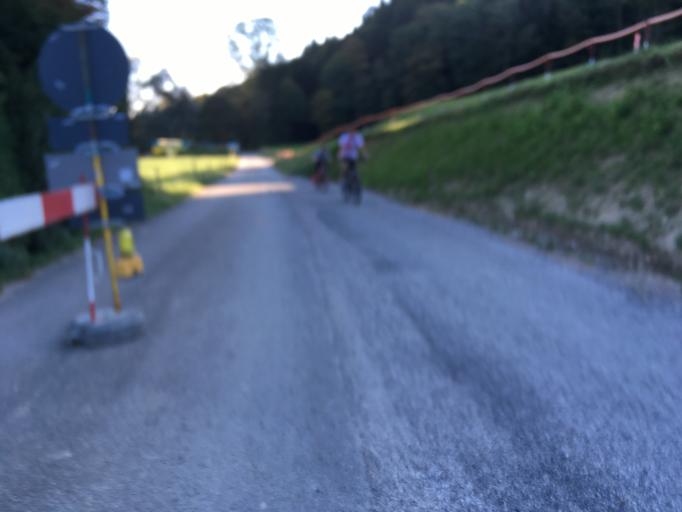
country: CH
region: Zurich
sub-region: Bezirk Buelach
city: Seglingen
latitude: 47.5619
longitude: 8.5461
